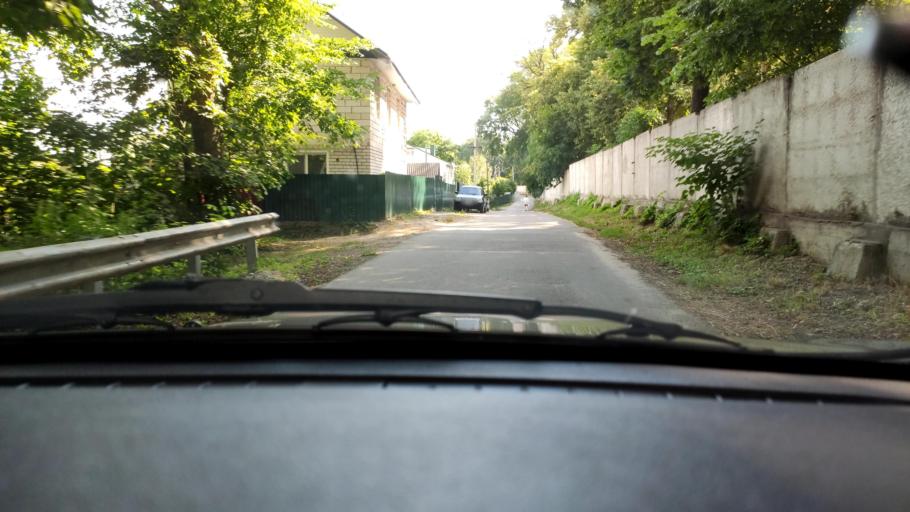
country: RU
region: Voronezj
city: Ramon'
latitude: 51.8238
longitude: 39.2700
